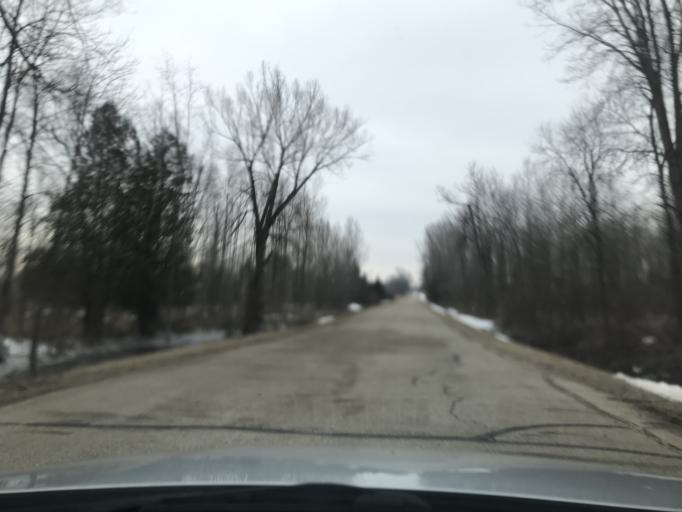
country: US
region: Wisconsin
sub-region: Marinette County
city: Peshtigo
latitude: 45.1291
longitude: -88.0076
